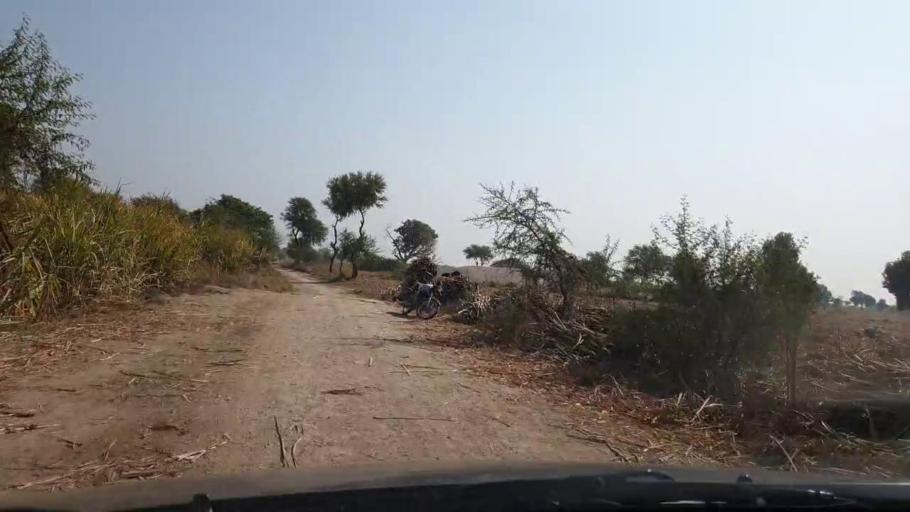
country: PK
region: Sindh
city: Jhol
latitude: 25.8590
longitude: 69.0035
